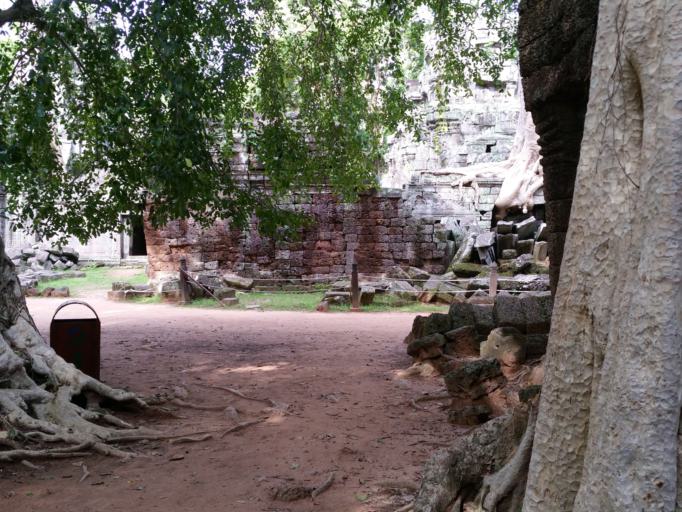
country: KH
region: Siem Reap
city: Siem Reap
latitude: 13.4349
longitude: 103.8890
